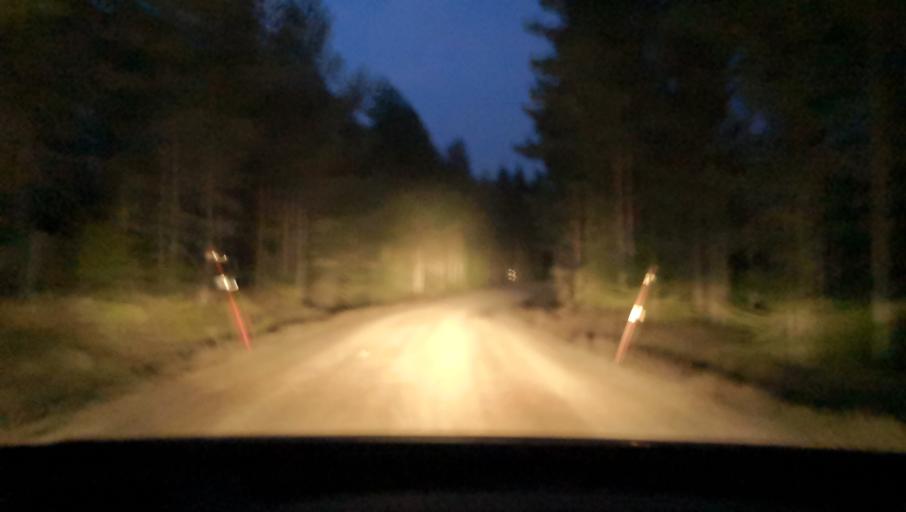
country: SE
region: OErebro
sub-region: Lindesbergs Kommun
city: Frovi
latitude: 59.6413
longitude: 15.4780
